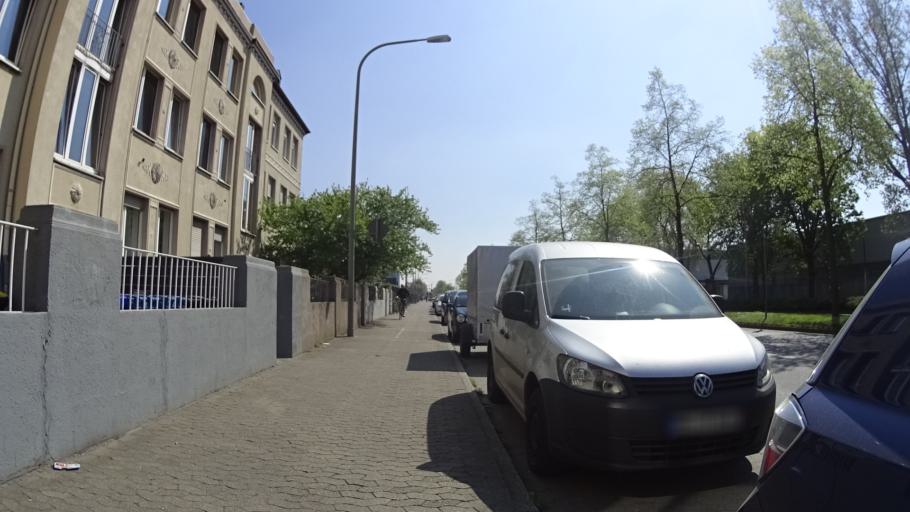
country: DE
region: North Rhine-Westphalia
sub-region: Regierungsbezirk Dusseldorf
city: Krefeld
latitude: 51.3440
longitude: 6.6574
